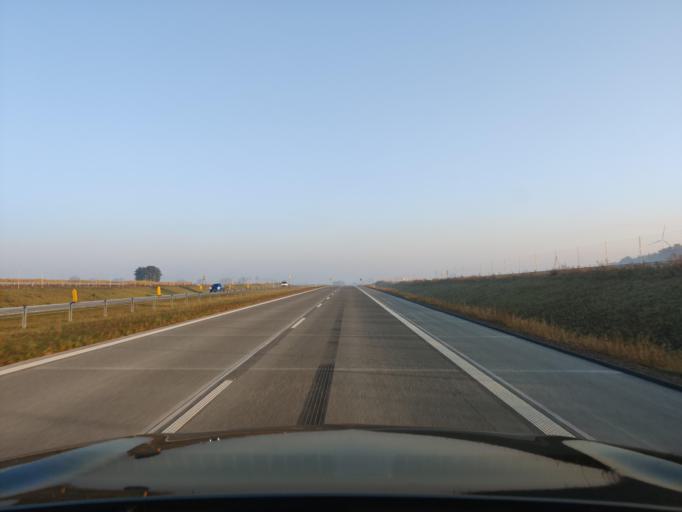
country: PL
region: Masovian Voivodeship
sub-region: Powiat mlawski
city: Wieczfnia Koscielna
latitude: 53.1637
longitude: 20.4263
